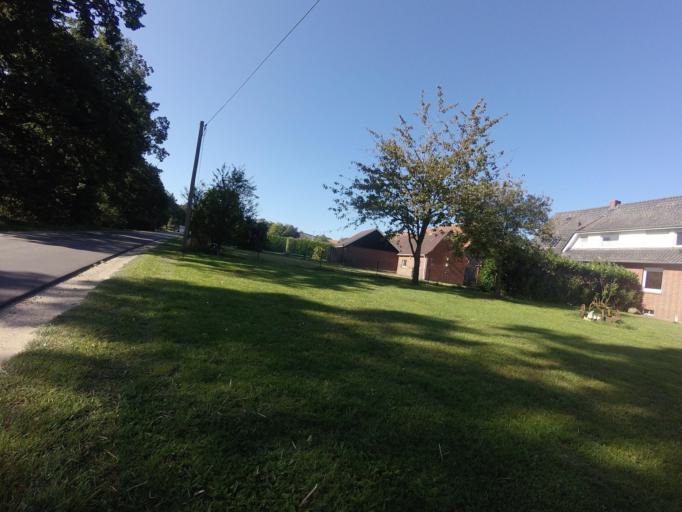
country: DE
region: Lower Saxony
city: Wielen
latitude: 52.5499
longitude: 6.7192
